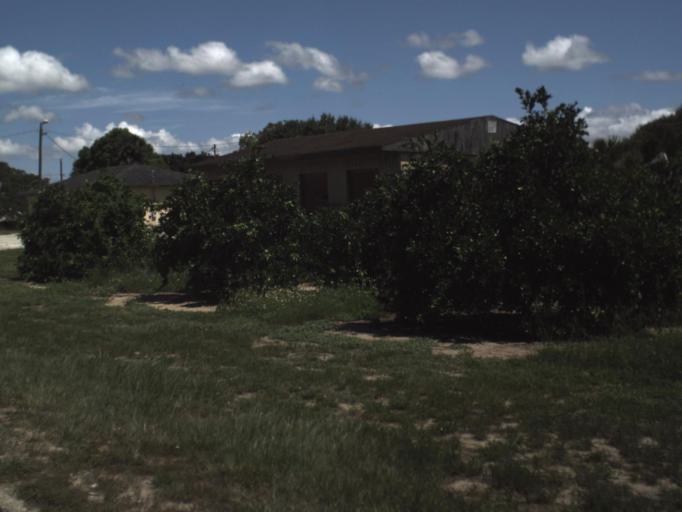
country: US
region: Florida
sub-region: Polk County
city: Frostproof
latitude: 27.7345
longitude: -81.5304
